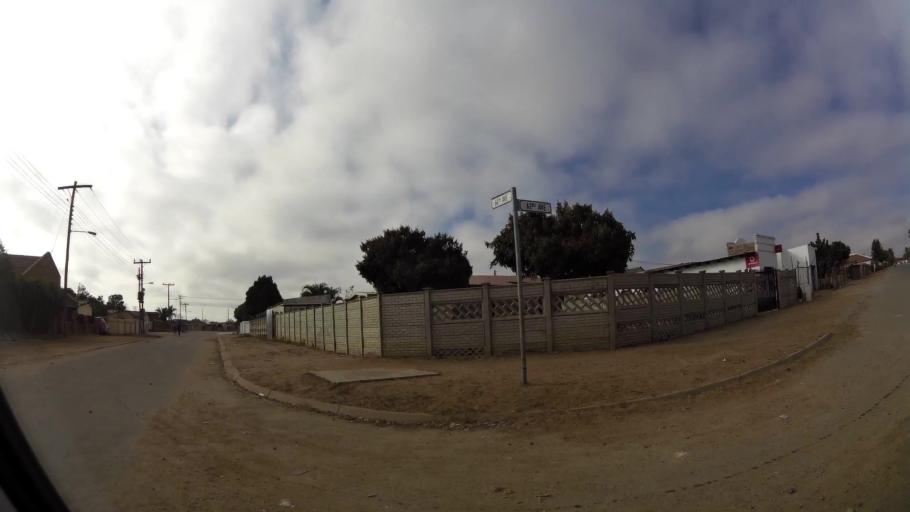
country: ZA
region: Limpopo
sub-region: Capricorn District Municipality
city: Polokwane
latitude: -23.8420
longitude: 29.3813
